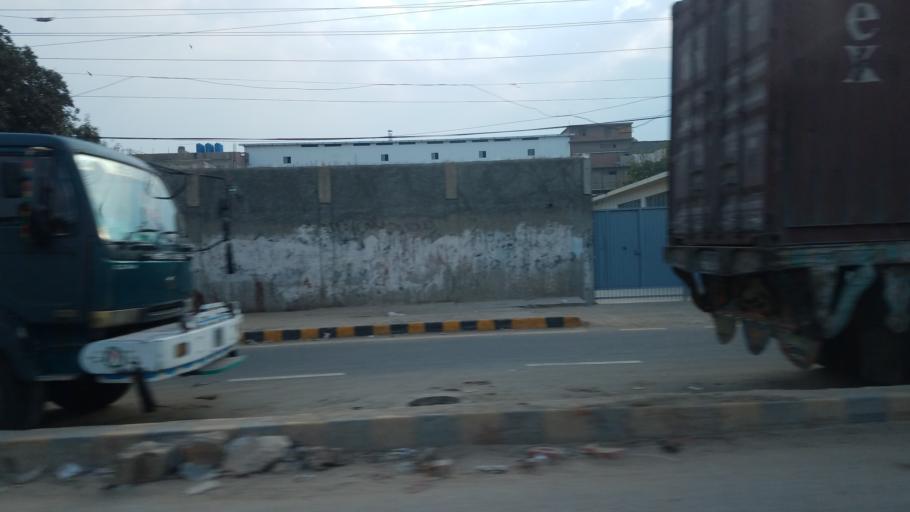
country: PK
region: Sindh
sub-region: Karachi District
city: Karachi
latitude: 24.9386
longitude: 67.0853
